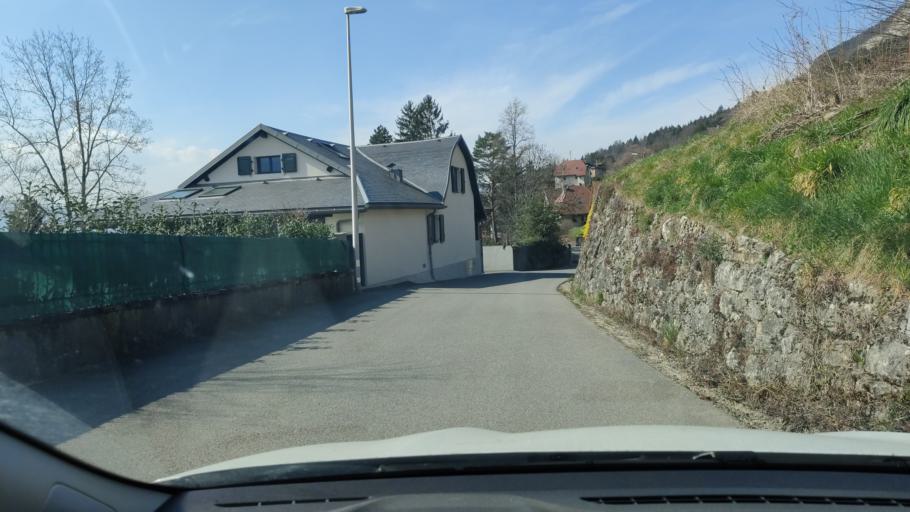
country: FR
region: Rhone-Alpes
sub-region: Departement de la Haute-Savoie
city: Bonneville
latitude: 46.0882
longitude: 6.4076
